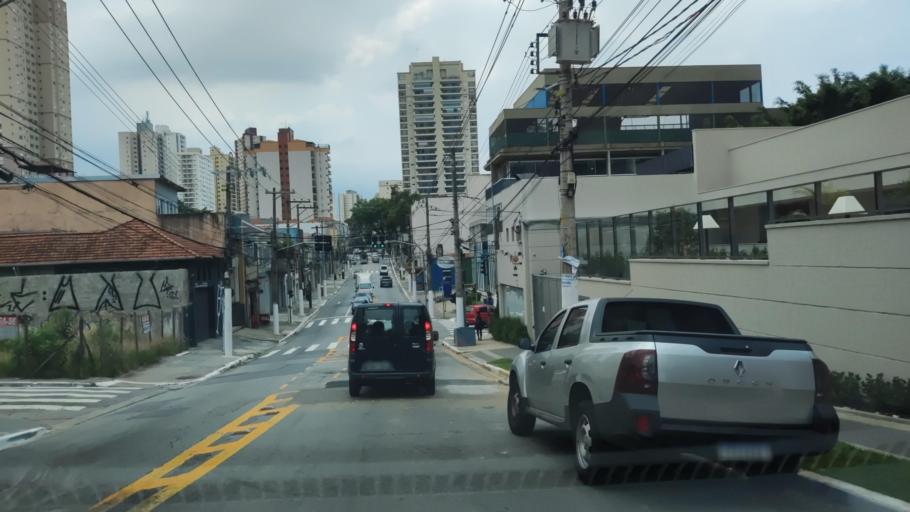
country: BR
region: Sao Paulo
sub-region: Sao Paulo
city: Sao Paulo
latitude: -23.5028
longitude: -46.6419
